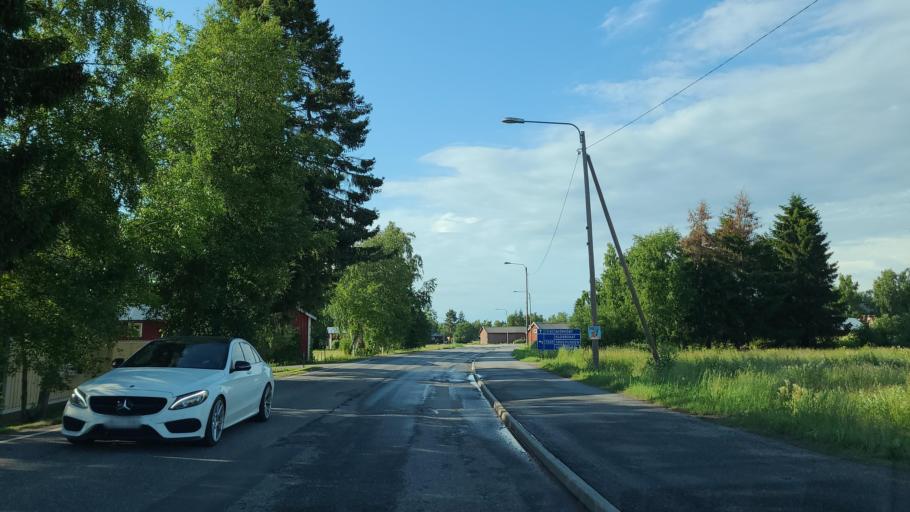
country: FI
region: Ostrobothnia
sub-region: Vaasa
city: Replot
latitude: 63.2288
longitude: 21.4104
